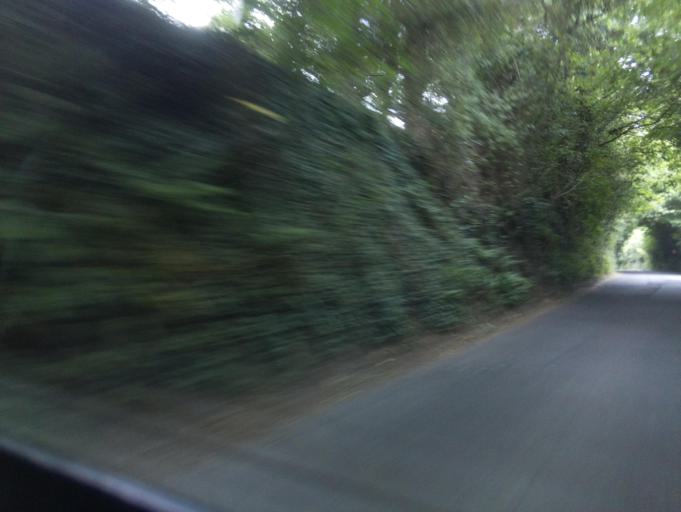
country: GB
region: England
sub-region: Dorset
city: Bridport
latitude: 50.7272
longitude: -2.7657
